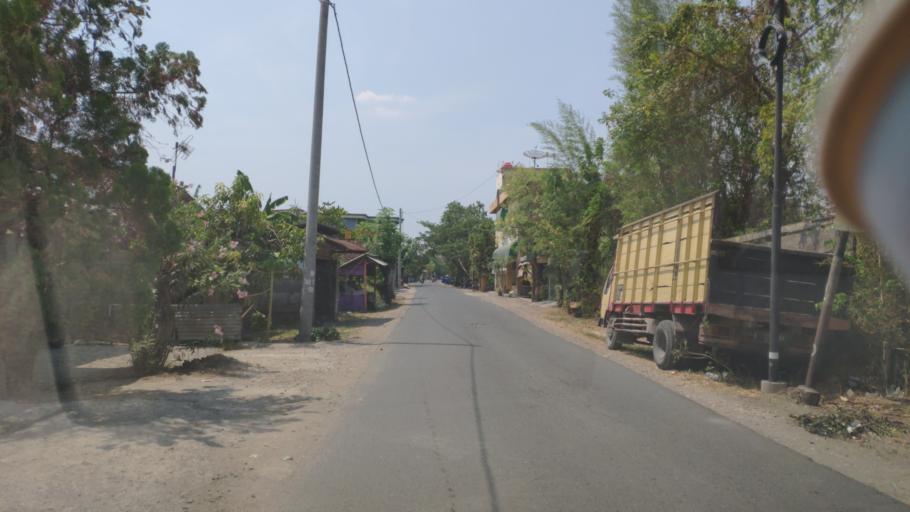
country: ID
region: Central Java
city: Wulung
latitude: -7.1886
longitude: 111.3965
